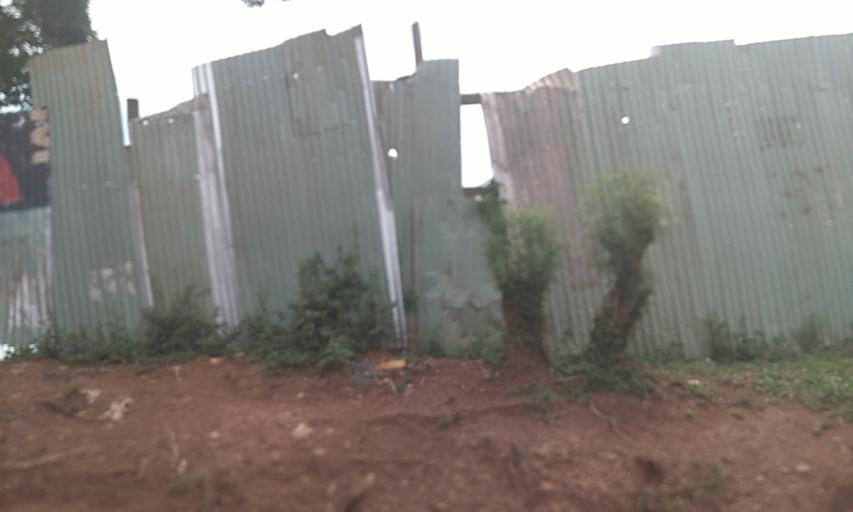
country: UG
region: Central Region
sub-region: Kampala District
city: Kampala
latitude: 0.3325
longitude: 32.6067
